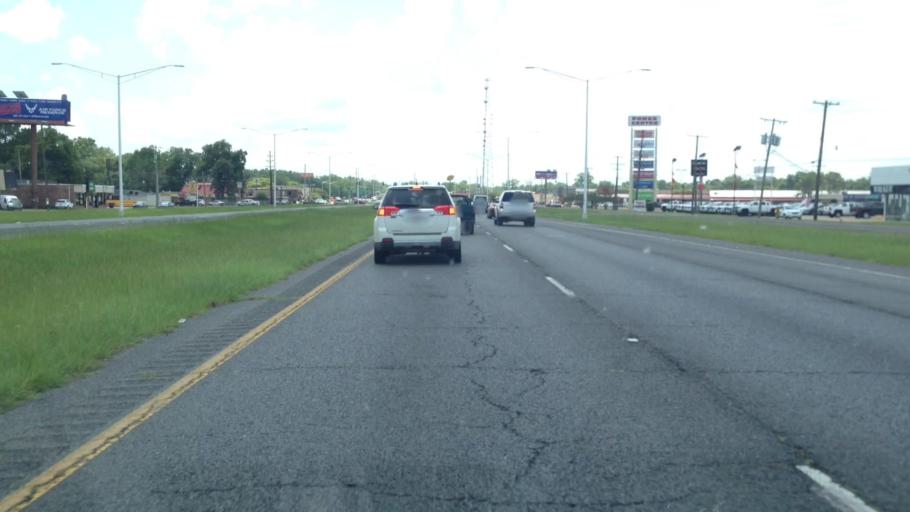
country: US
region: Louisiana
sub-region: Rapides Parish
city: Alexandria
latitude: 31.2812
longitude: -92.4730
